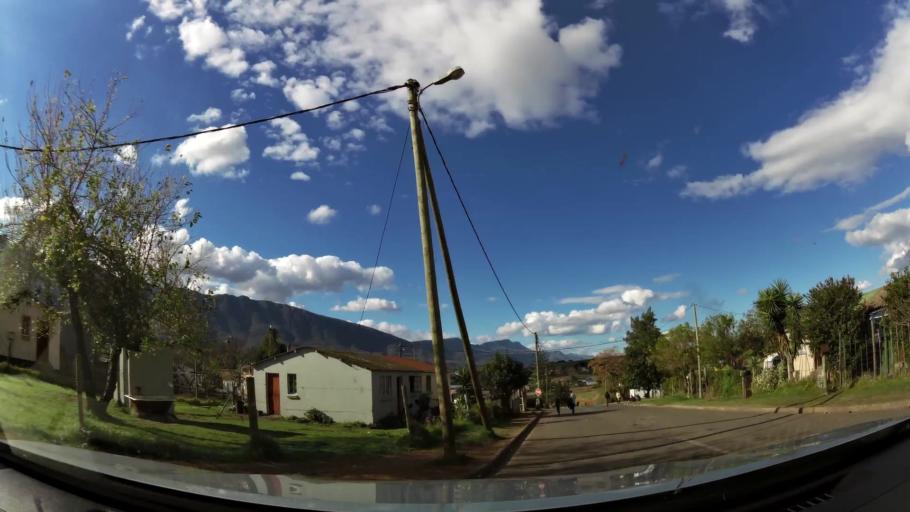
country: ZA
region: Western Cape
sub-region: Overberg District Municipality
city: Swellendam
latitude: -34.0343
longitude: 20.4466
